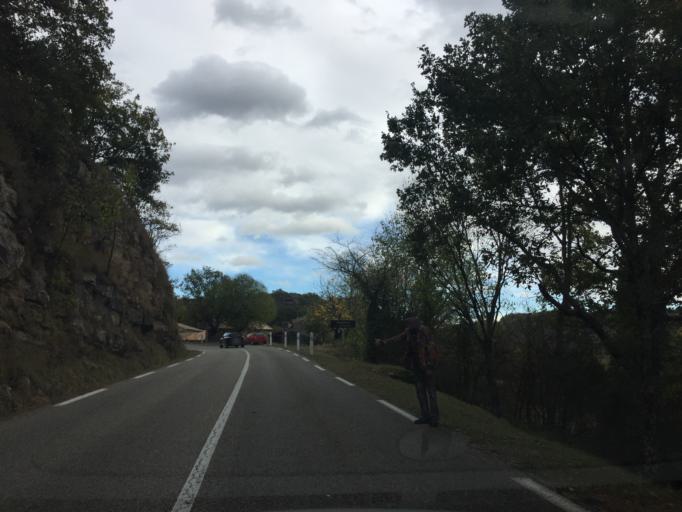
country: FR
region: Rhone-Alpes
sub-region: Departement de l'Ardeche
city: Les Vans
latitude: 44.4158
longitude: 4.1705
